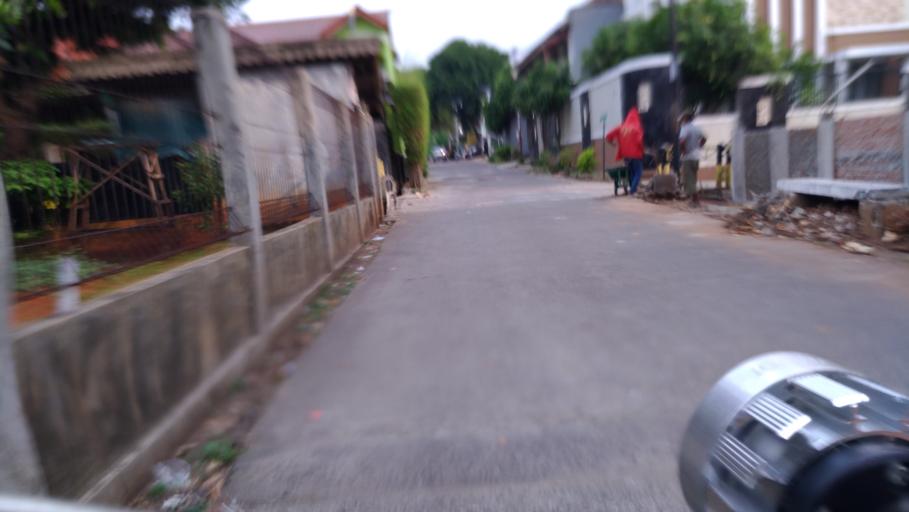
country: ID
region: West Java
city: Depok
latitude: -6.3621
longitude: 106.8661
